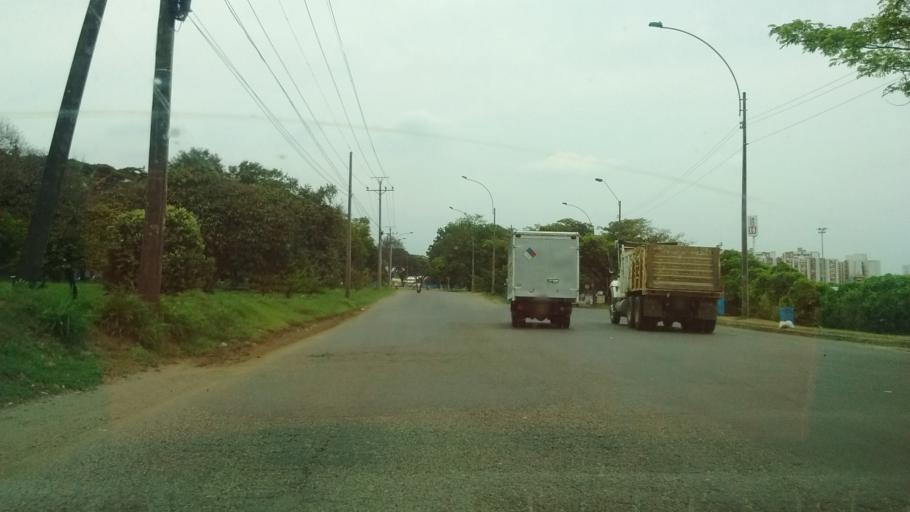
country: CO
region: Valle del Cauca
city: Cali
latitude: 3.3654
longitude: -76.5247
